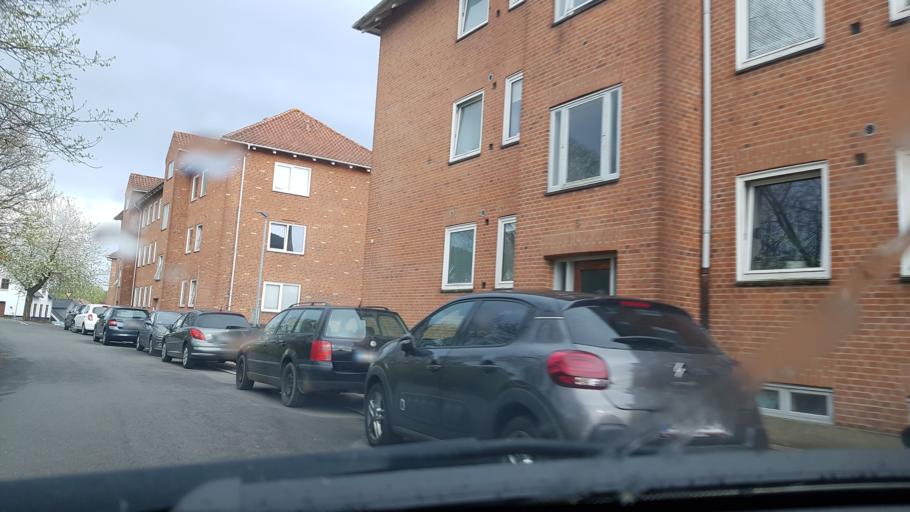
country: DK
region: South Denmark
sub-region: Kolding Kommune
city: Kolding
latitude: 55.4966
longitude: 9.4691
